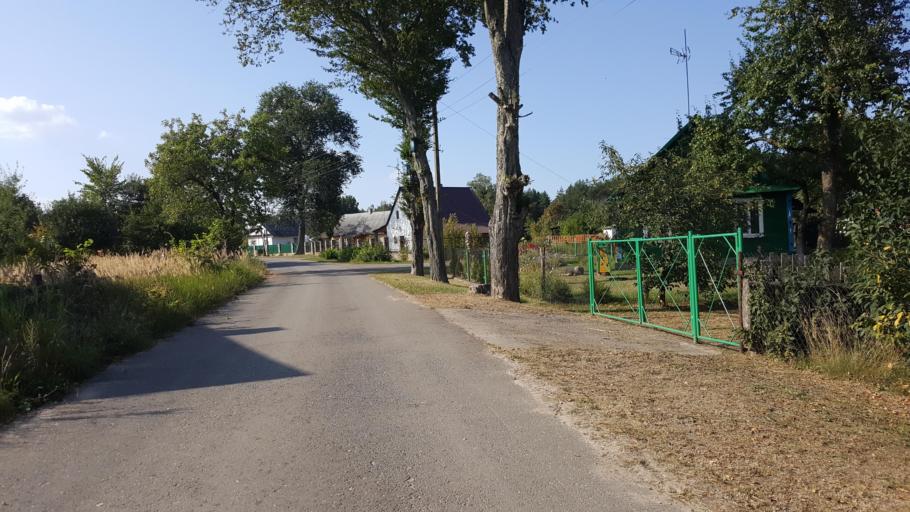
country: BY
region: Brest
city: Kamyanyuki
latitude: 52.5497
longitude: 23.6527
